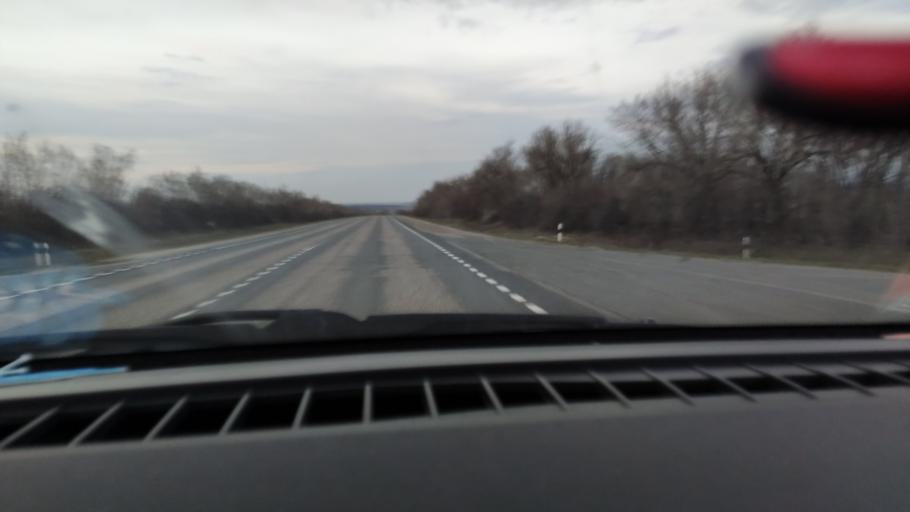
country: RU
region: Saratov
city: Sinodskoye
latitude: 51.9537
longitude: 46.6119
